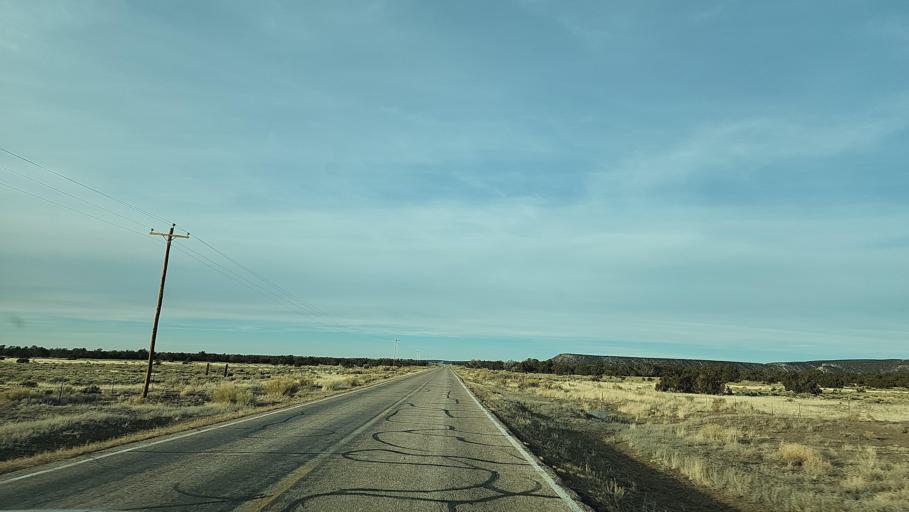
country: US
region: New Mexico
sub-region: McKinley County
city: Black Rock
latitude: 34.4408
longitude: -108.4273
